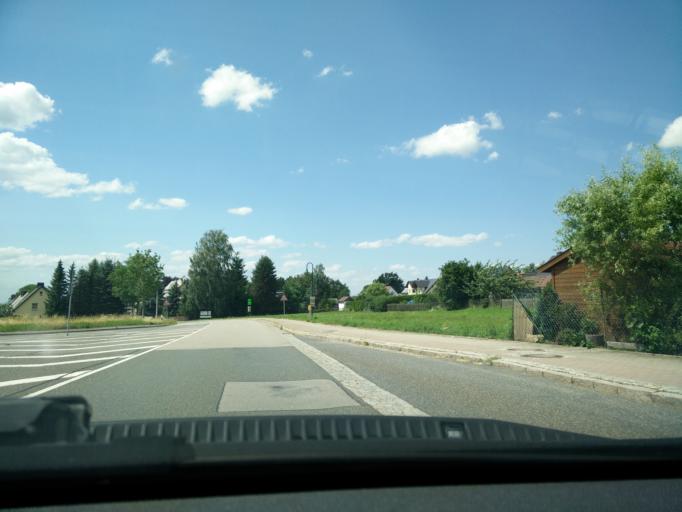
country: DE
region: Saxony
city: Muhlau
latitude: 50.8994
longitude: 12.7683
